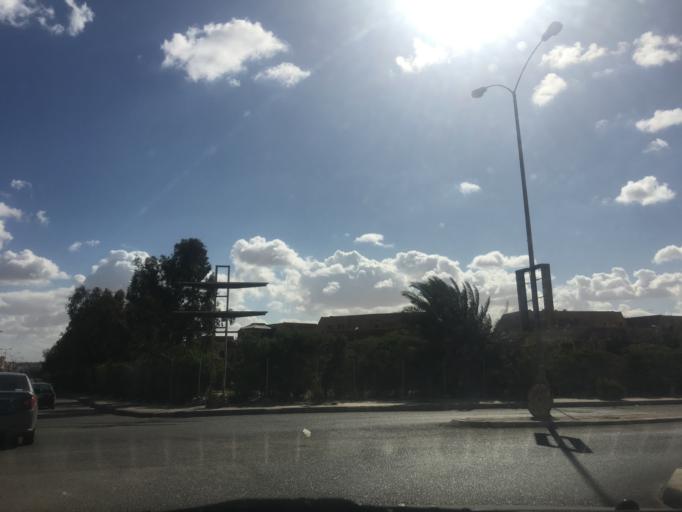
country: EG
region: Al Jizah
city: Madinat Sittah Uktubar
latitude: 29.9993
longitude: 30.9750
